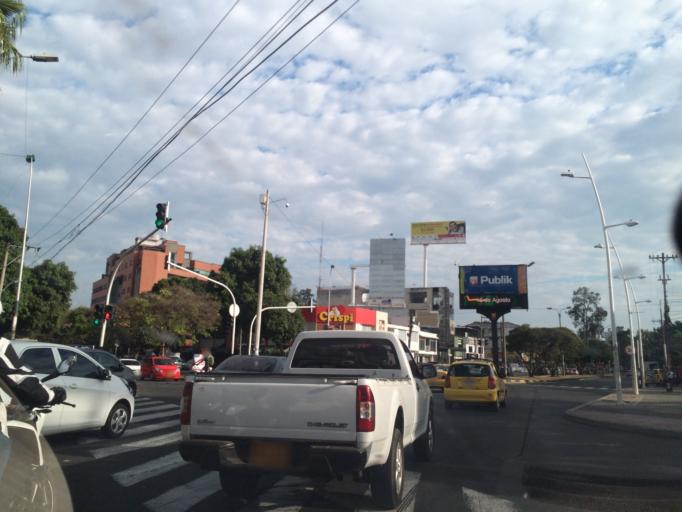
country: CO
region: Valle del Cauca
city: Cali
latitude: 3.4286
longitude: -76.5391
